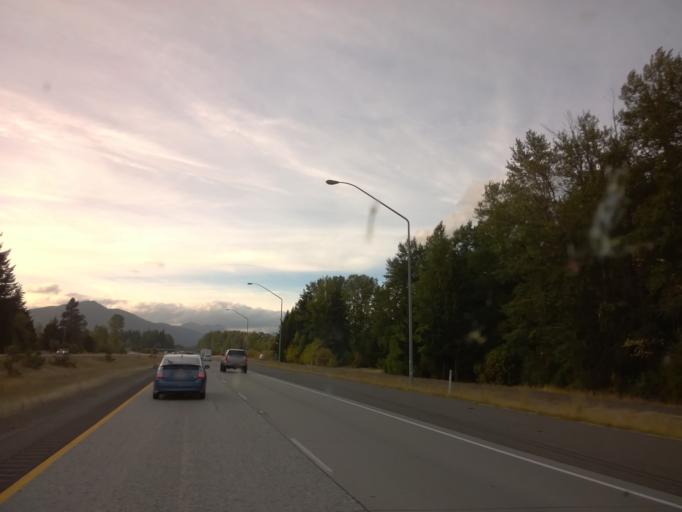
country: US
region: Washington
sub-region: Kittitas County
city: Cle Elum
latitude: 47.2311
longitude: -121.1671
